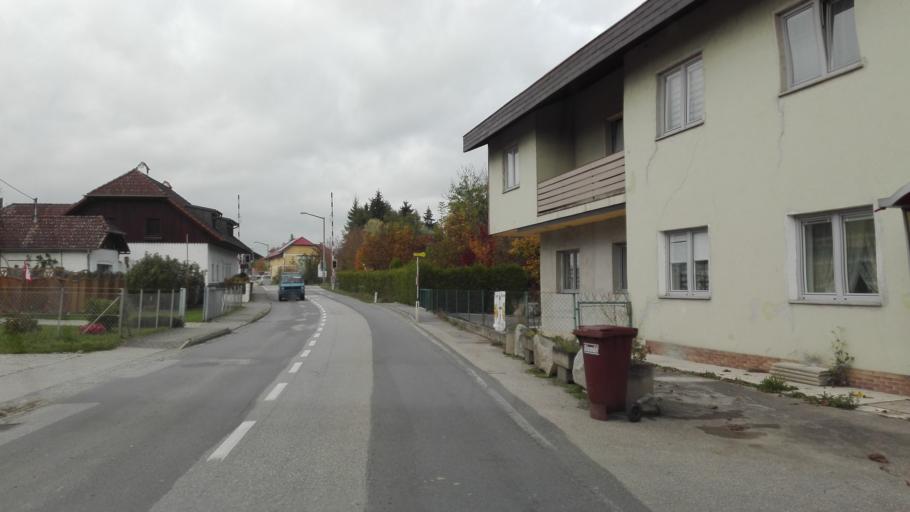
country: AT
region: Upper Austria
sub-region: Politischer Bezirk Urfahr-Umgebung
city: Feldkirchen an der Donau
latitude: 48.3518
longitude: 13.9949
